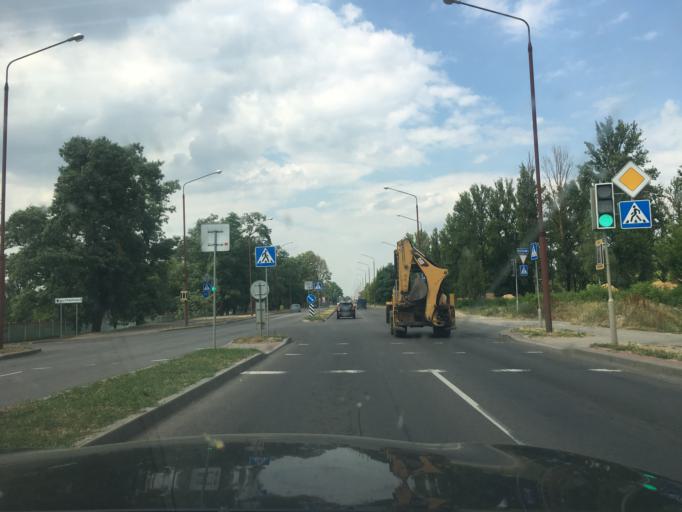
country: BY
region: Brest
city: Brest
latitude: 52.1288
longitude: 23.6736
